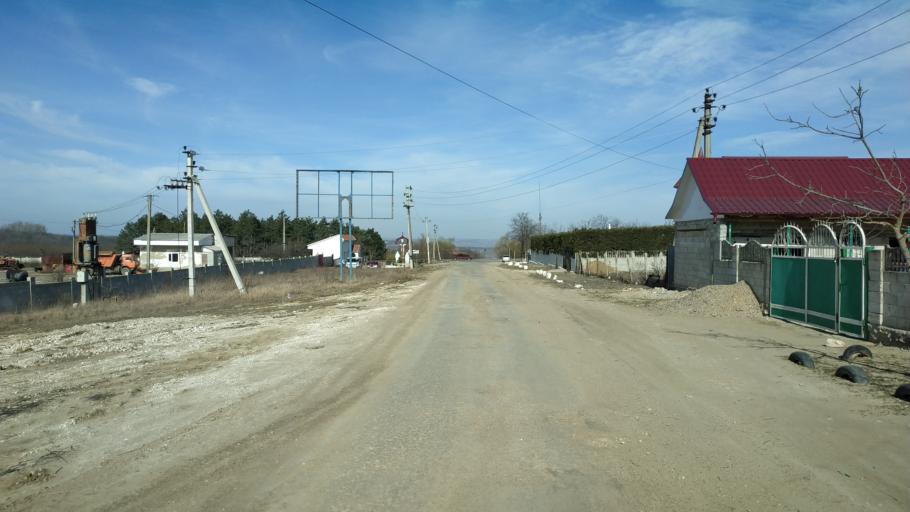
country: MD
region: Nisporeni
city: Nisporeni
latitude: 47.1034
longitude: 28.2958
